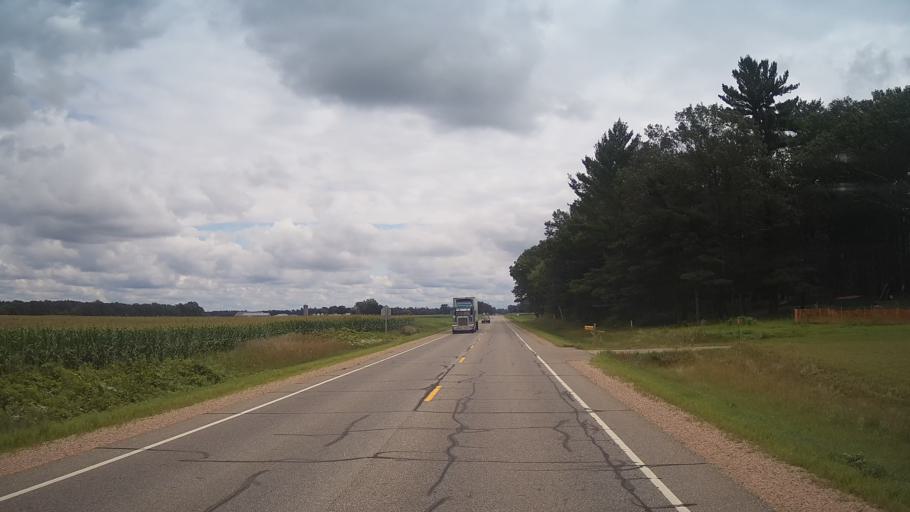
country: US
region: Wisconsin
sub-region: Adams County
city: Friendship
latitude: 44.0393
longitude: -89.9250
